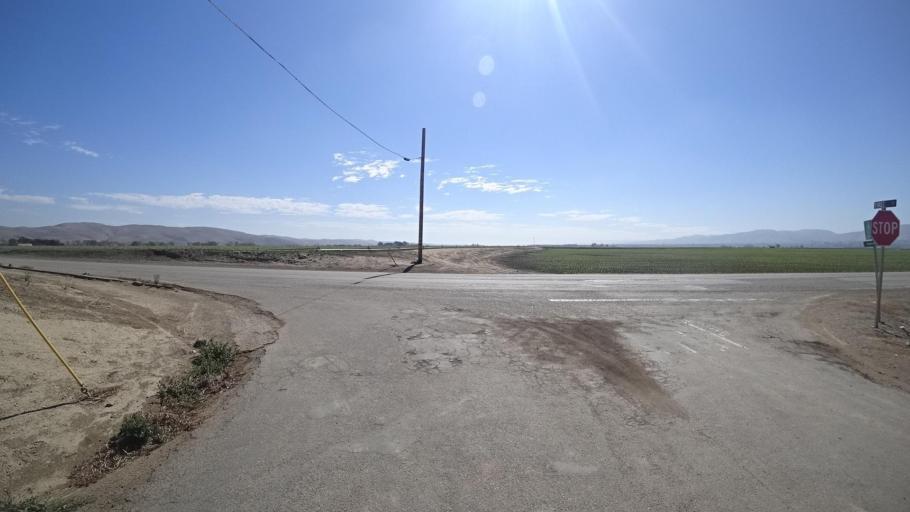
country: US
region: California
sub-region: Monterey County
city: Greenfield
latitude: 36.3341
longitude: -121.2204
